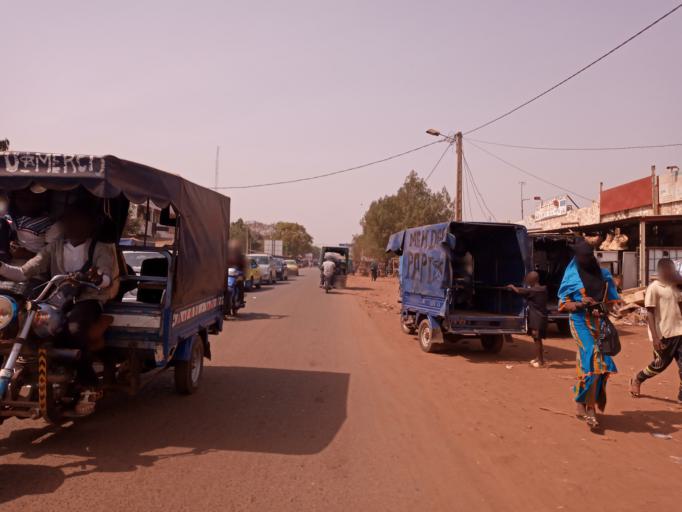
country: ML
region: Bamako
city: Bamako
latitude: 12.5963
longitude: -7.9606
